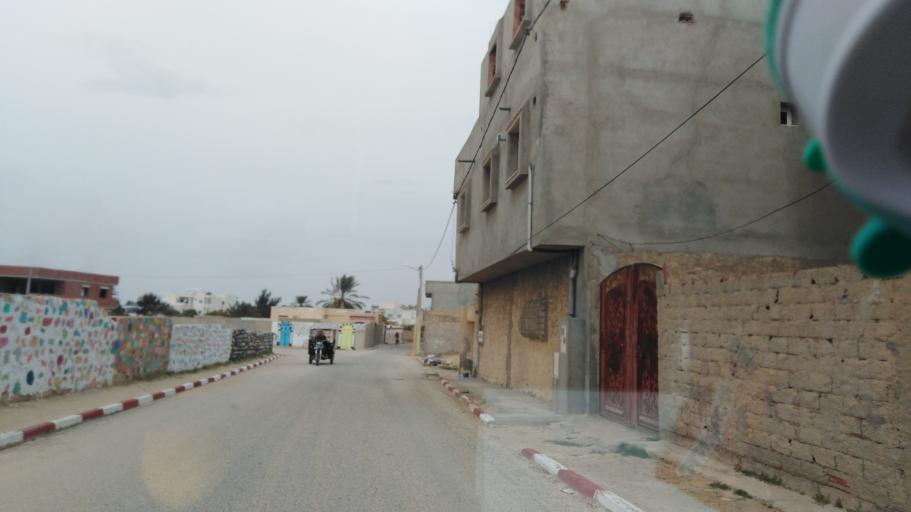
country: TN
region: Qabis
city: Gabes
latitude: 33.9564
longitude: 10.0027
